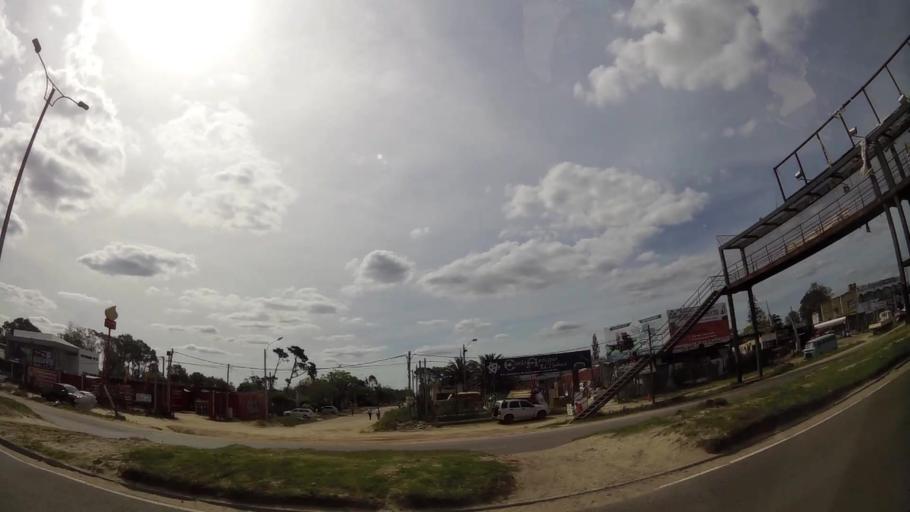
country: UY
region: Canelones
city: Colonia Nicolich
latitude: -34.8260
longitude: -55.9656
